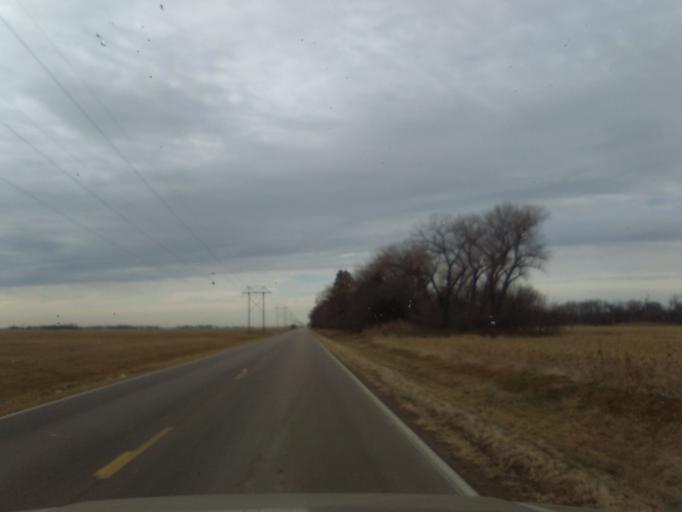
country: US
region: Nebraska
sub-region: Buffalo County
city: Gibbon
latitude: 40.6550
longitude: -98.8107
